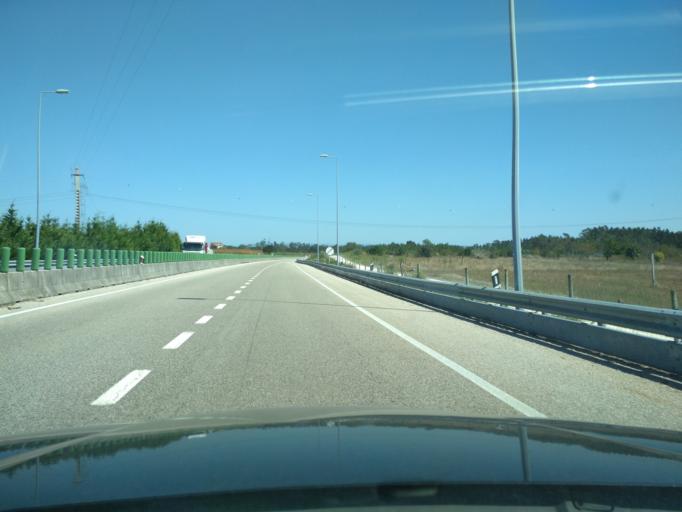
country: PT
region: Leiria
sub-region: Pombal
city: Lourical
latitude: 39.9885
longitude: -8.7848
